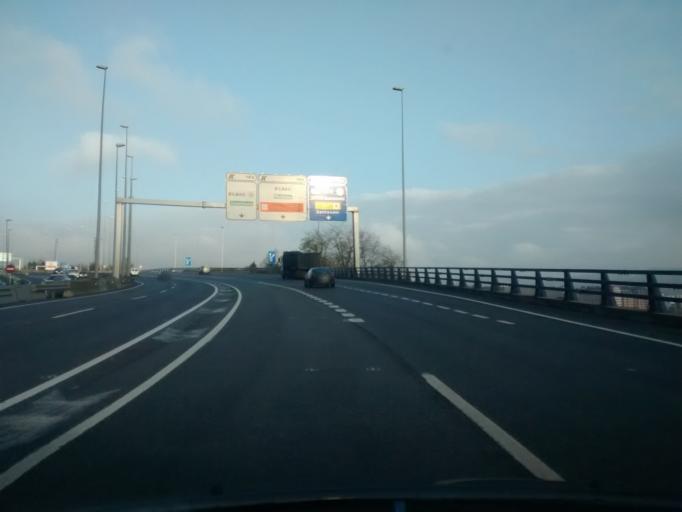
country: ES
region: Basque Country
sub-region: Bizkaia
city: Santutxu
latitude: 43.2415
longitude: -2.9273
